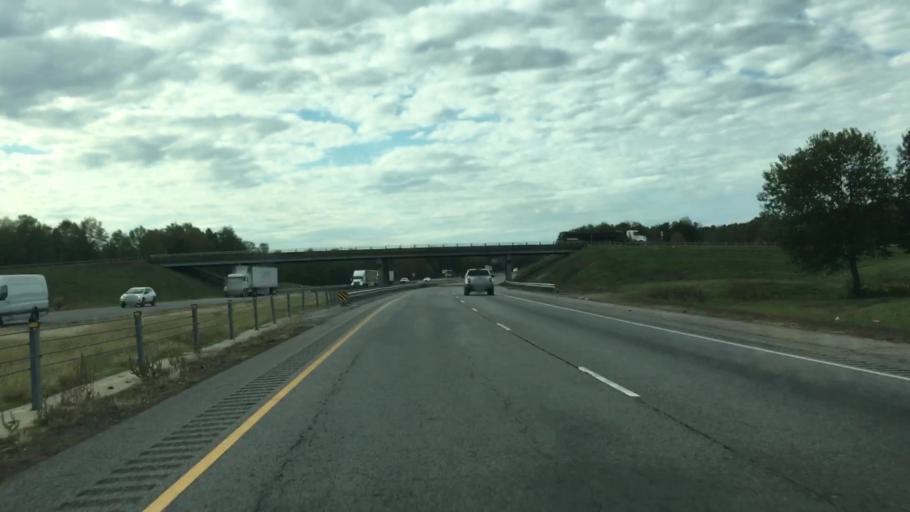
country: US
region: Arkansas
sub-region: Conway County
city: Morrilton
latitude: 35.1749
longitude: -92.7429
